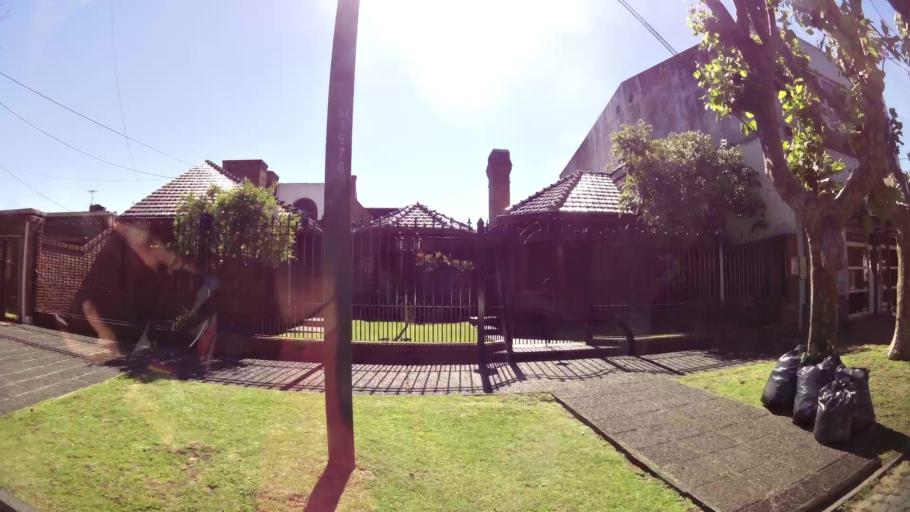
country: AR
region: Buenos Aires
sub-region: Partido de Lomas de Zamora
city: Lomas de Zamora
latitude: -34.7537
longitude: -58.4115
